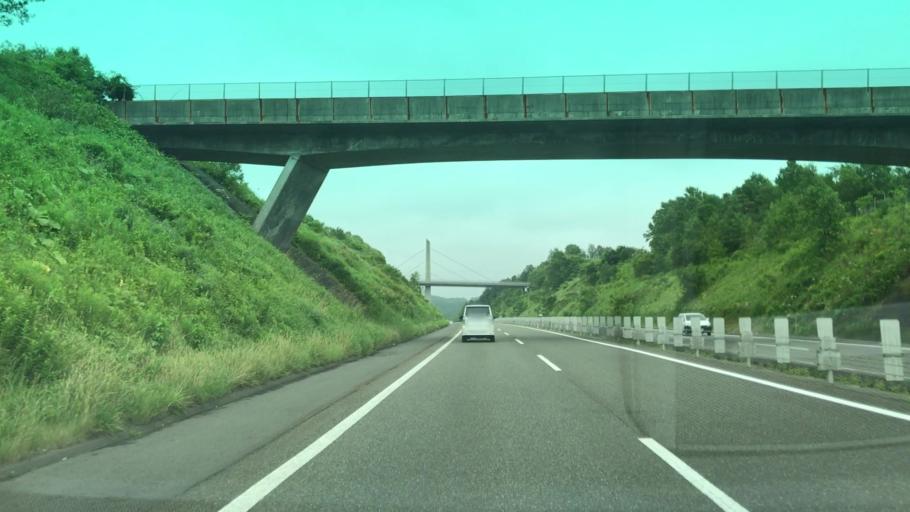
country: JP
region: Hokkaido
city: Tomakomai
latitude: 42.6214
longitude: 141.4779
